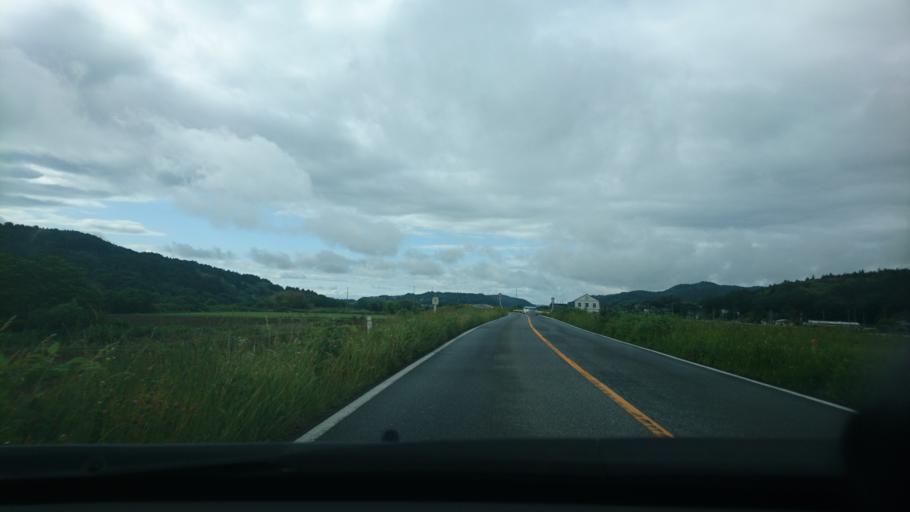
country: JP
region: Miyagi
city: Wakuya
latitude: 38.6372
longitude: 141.2887
